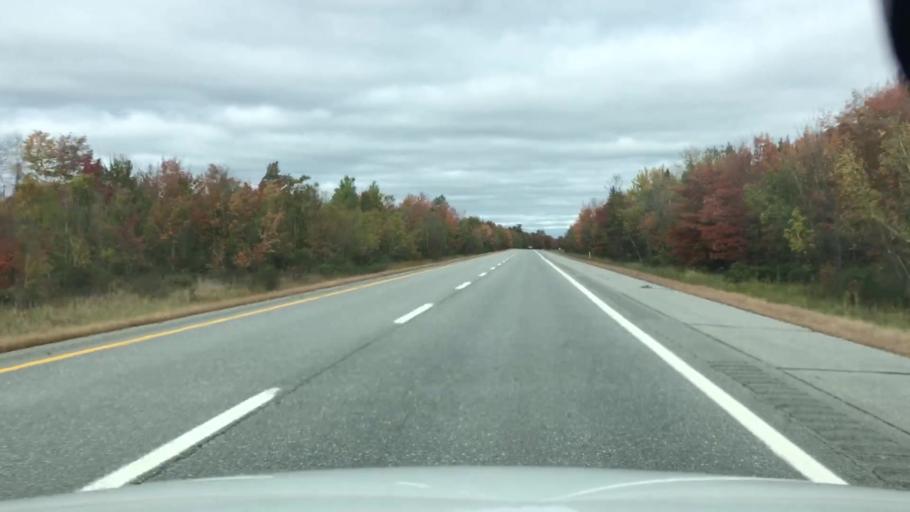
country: US
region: Maine
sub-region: Waldo County
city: Burnham
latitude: 44.6885
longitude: -69.4719
